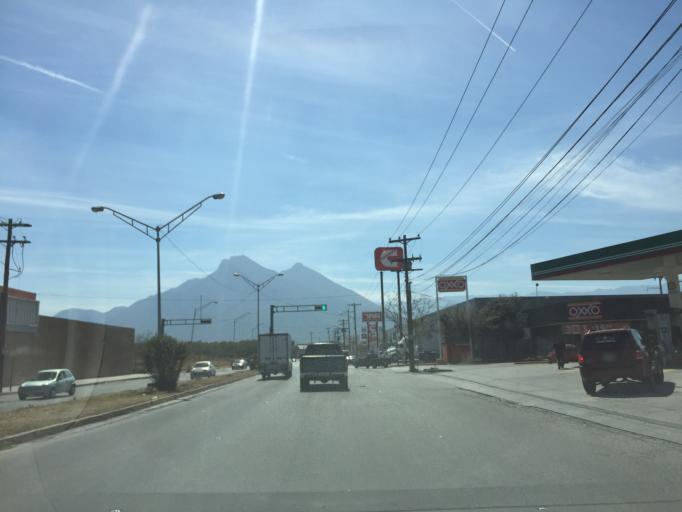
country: MX
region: Nuevo Leon
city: Guadalupe
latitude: 25.7013
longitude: -100.2399
